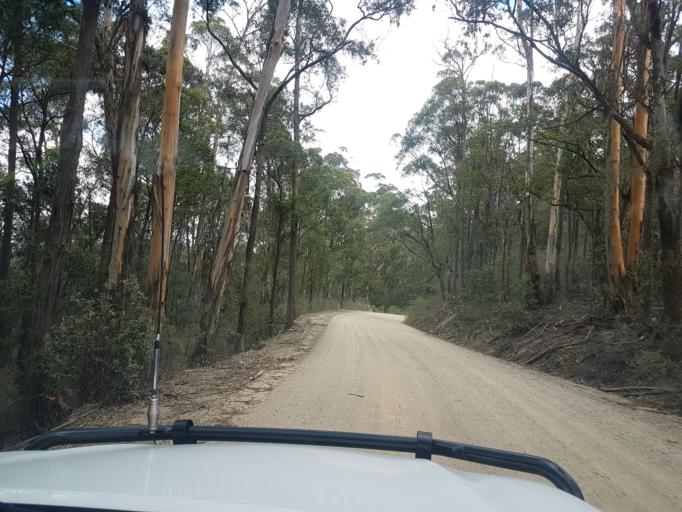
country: AU
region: Victoria
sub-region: East Gippsland
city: Bairnsdale
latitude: -37.6907
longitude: 147.5643
